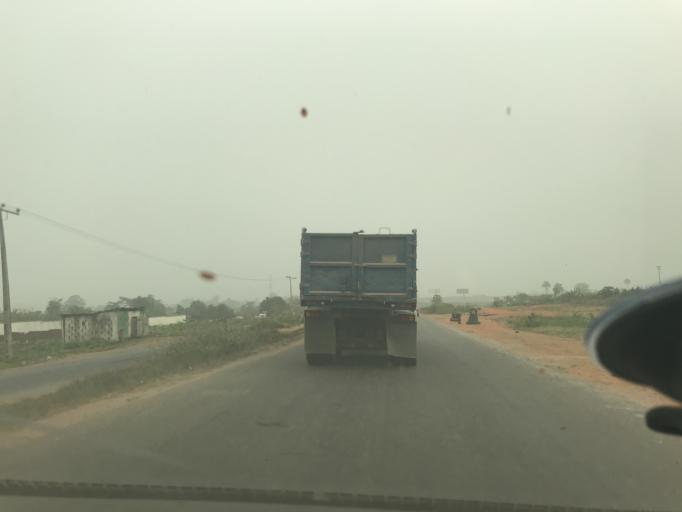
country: NG
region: Ogun
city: Shagamu
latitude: 6.8873
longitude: 3.5719
